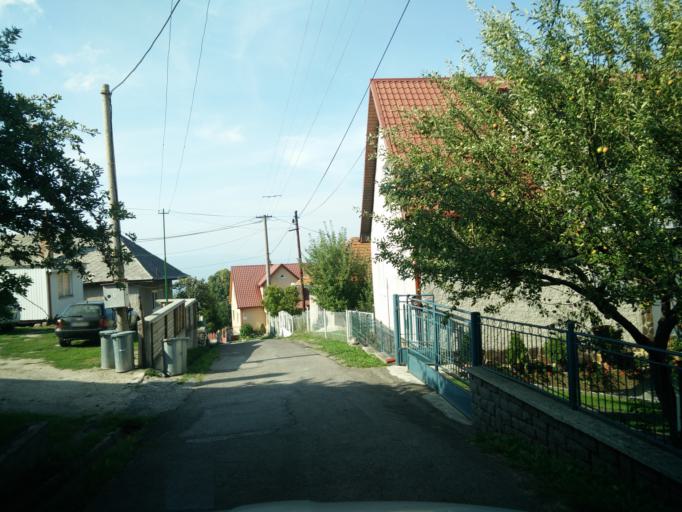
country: SK
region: Nitriansky
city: Prievidza
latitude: 48.6859
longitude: 18.6318
